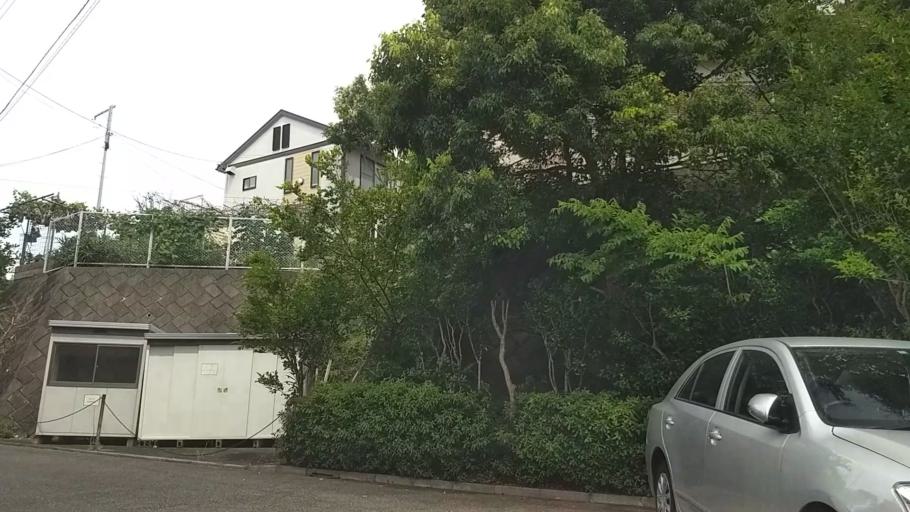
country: JP
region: Kanagawa
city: Yokohama
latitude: 35.4446
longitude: 139.6008
